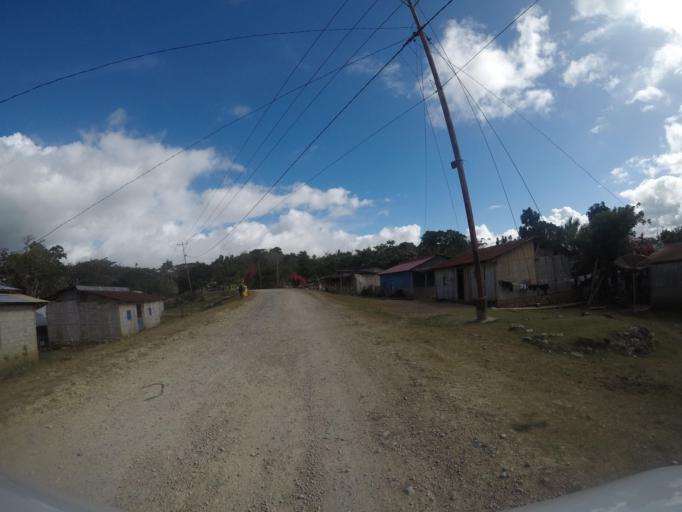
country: TL
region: Lautem
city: Lospalos
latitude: -8.5742
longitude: 126.8836
